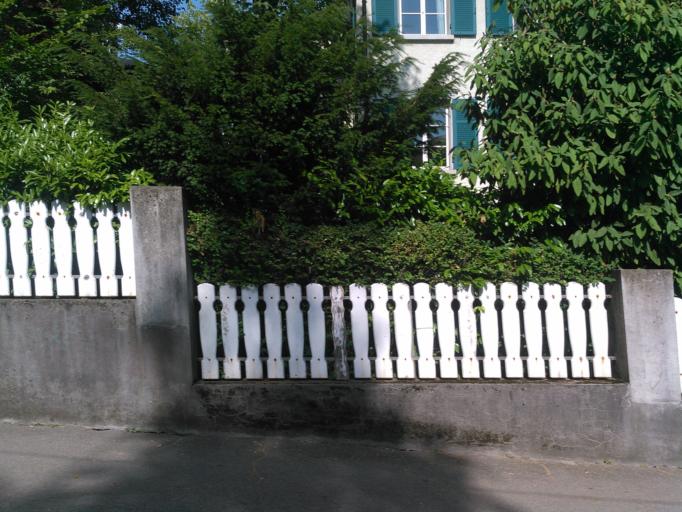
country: CH
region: Zurich
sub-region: Bezirk Zuerich
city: Zuerich (Kreis 7) / Fluntern
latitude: 47.3783
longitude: 8.5594
